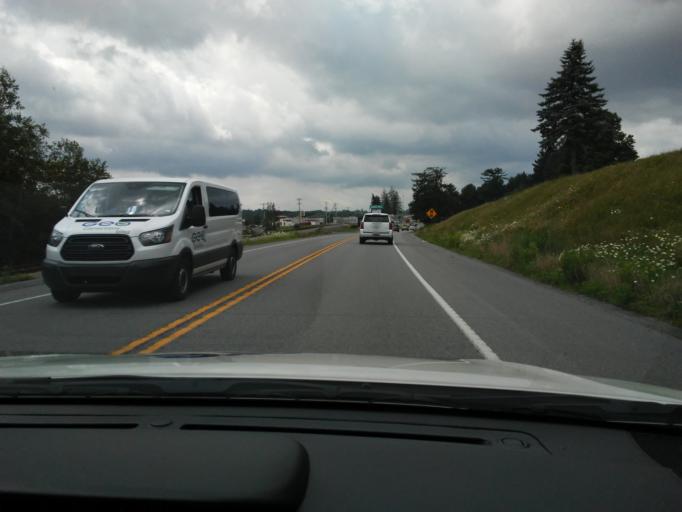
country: US
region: Pennsylvania
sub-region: Clearfield County
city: DuBois
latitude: 41.1233
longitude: -78.7211
